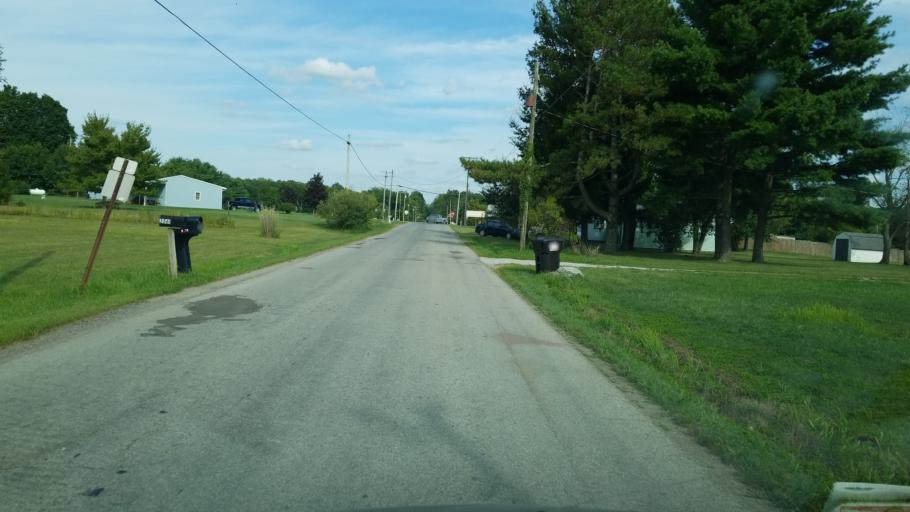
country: US
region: Ohio
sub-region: Morrow County
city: Cardington
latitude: 40.4640
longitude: -82.8425
